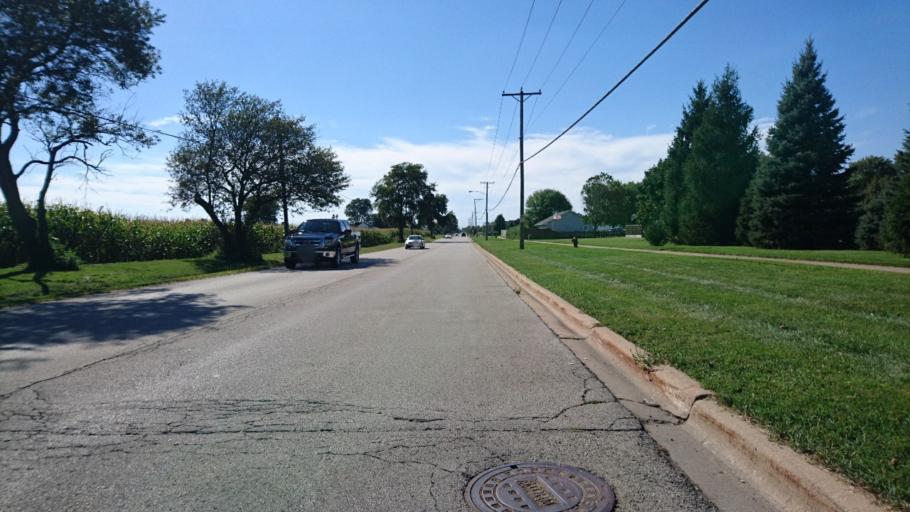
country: US
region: Illinois
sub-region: Will County
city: New Lenox
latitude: 41.5117
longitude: -87.9977
